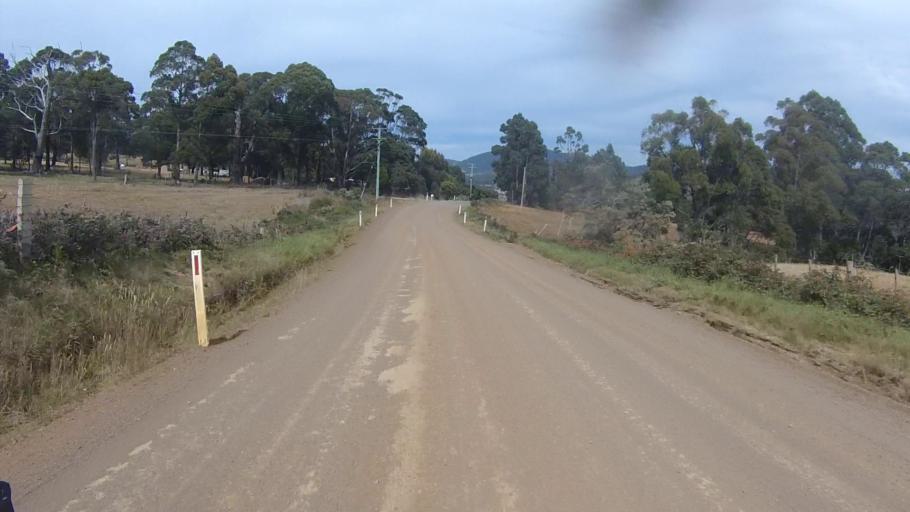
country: AU
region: Tasmania
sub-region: Sorell
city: Sorell
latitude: -42.7781
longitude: 147.8170
